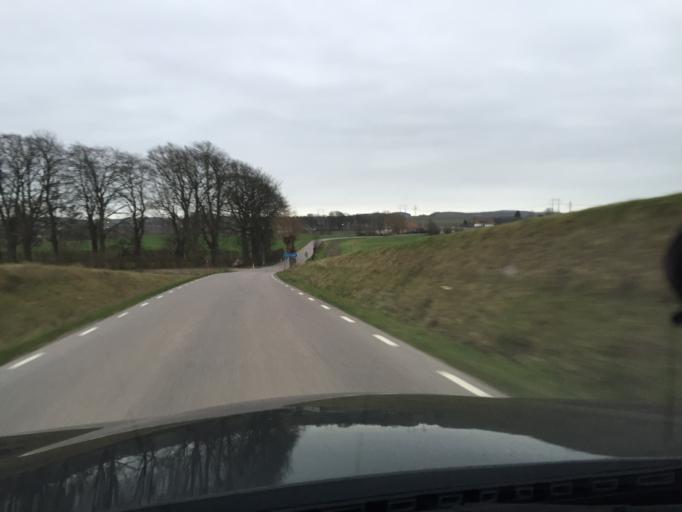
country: SE
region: Skane
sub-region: Malmo
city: Oxie
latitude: 55.5756
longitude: 13.1562
